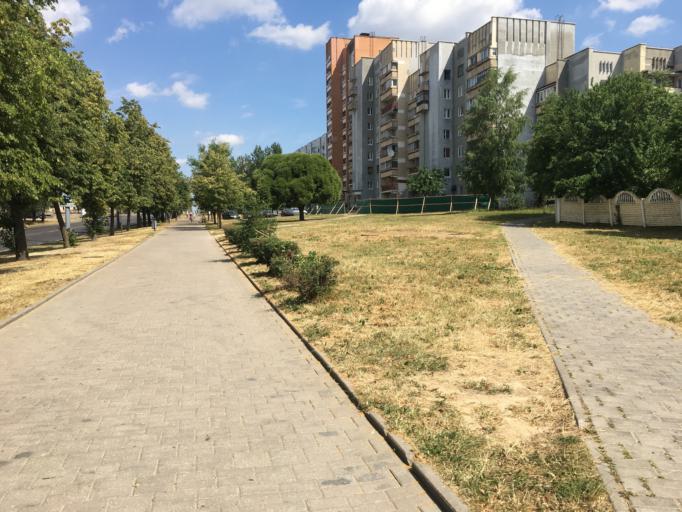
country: BY
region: Grodnenskaya
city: Hrodna
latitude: 53.7090
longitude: 23.8400
